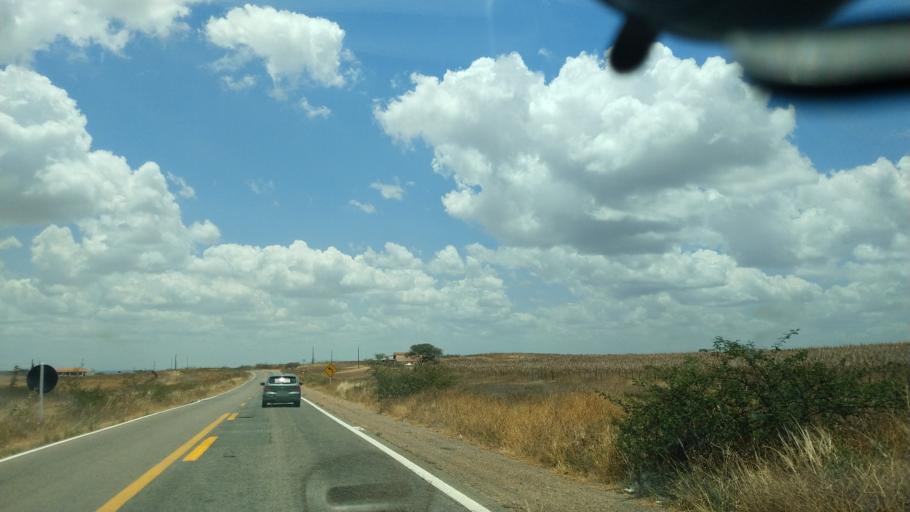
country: BR
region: Rio Grande do Norte
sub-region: Cerro Cora
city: Cerro Cora
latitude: -6.1897
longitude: -36.2522
